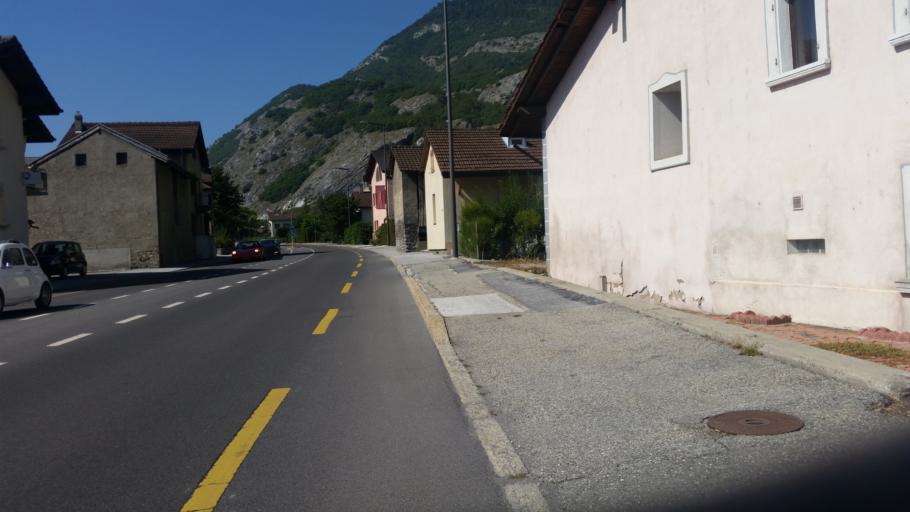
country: CH
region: Valais
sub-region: Conthey District
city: Ardon
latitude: 46.2195
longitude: 7.2644
